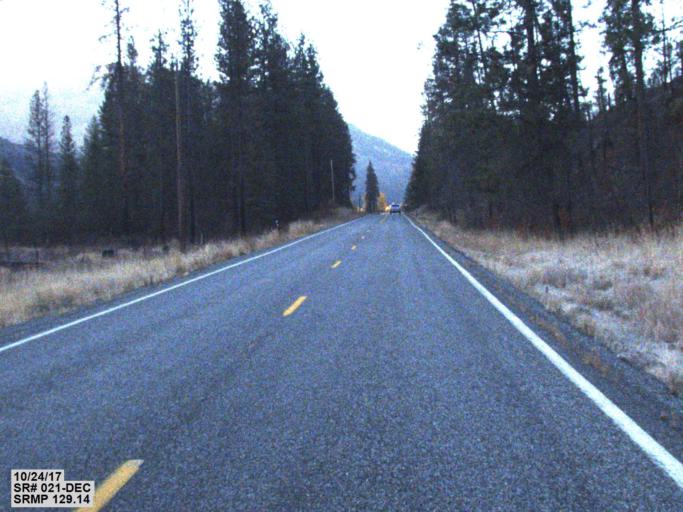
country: US
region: Washington
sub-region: Okanogan County
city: Coulee Dam
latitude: 48.2485
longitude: -118.6929
